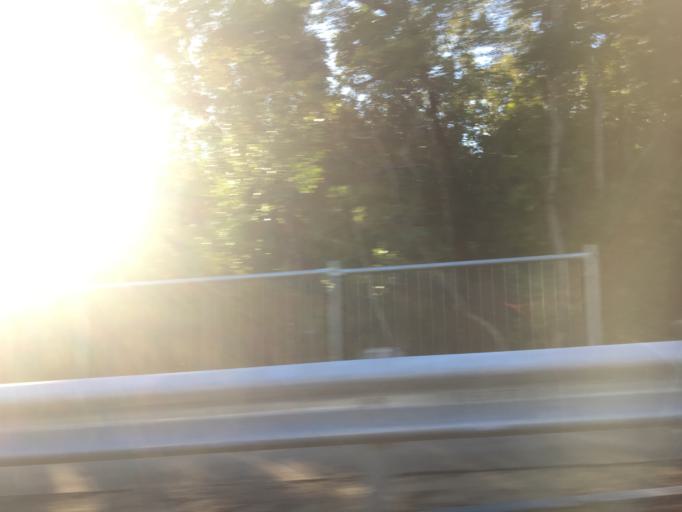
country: AU
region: Queensland
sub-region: Cairns
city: Yorkeys Knob
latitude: -16.8008
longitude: 145.7070
